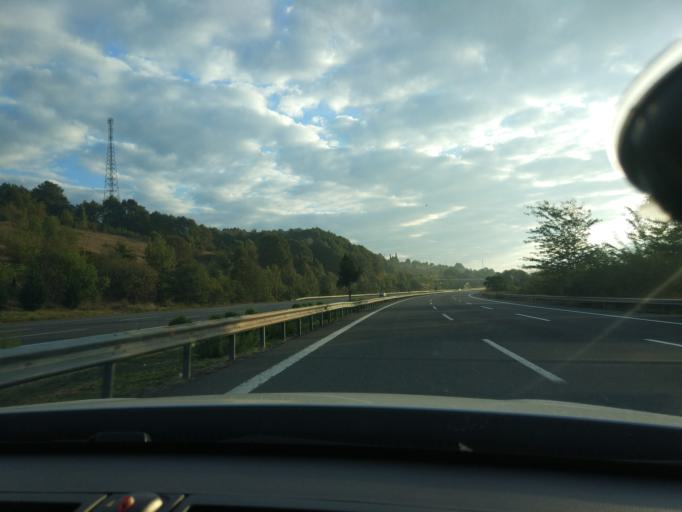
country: TR
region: Sakarya
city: Hendek
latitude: 40.7692
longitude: 30.7652
